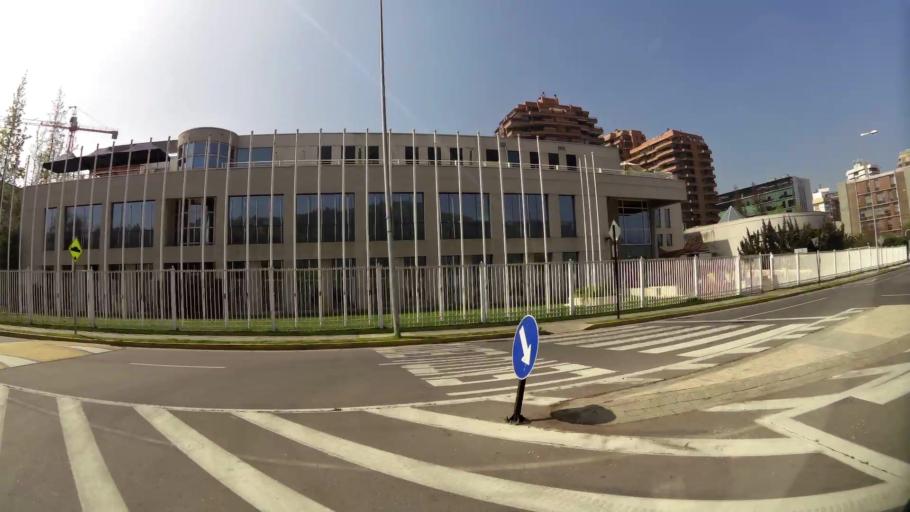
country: CL
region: Santiago Metropolitan
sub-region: Provincia de Santiago
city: Villa Presidente Frei, Nunoa, Santiago, Chile
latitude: -33.4048
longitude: -70.6008
